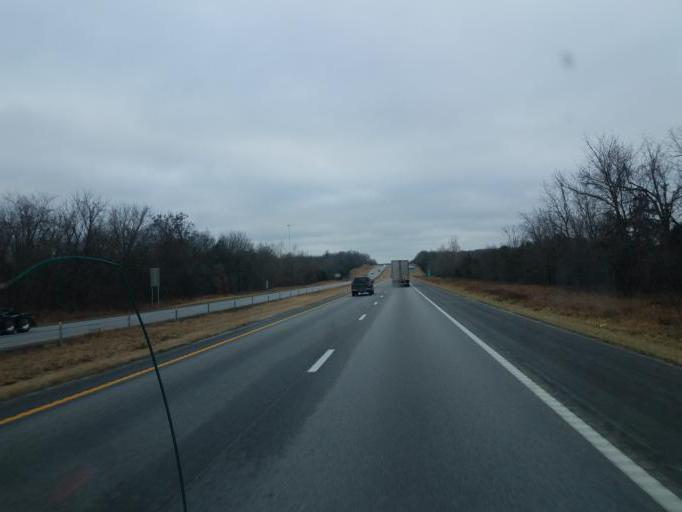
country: US
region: Missouri
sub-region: Webster County
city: Marshfield
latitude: 37.4824
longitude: -92.8530
